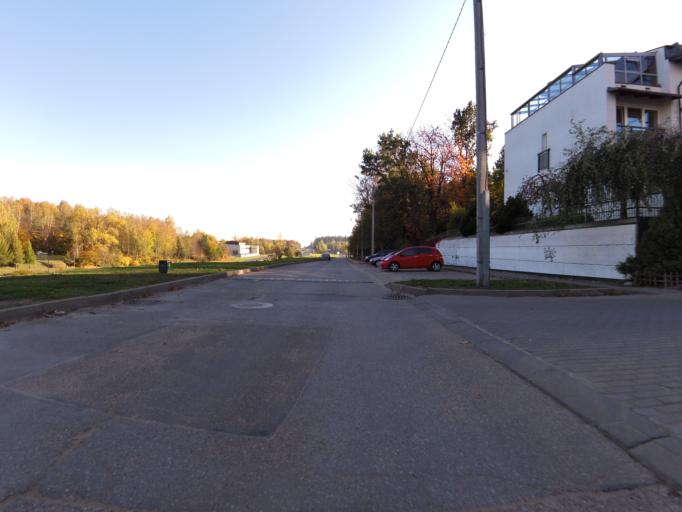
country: LT
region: Vilnius County
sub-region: Vilnius
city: Fabijoniskes
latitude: 54.7415
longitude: 25.2628
